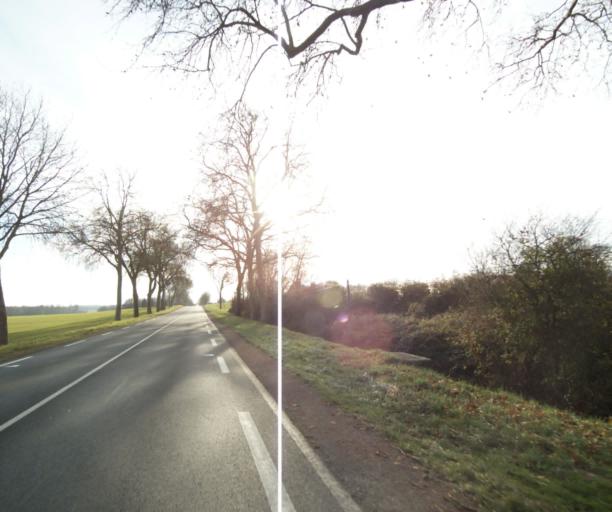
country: FR
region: Poitou-Charentes
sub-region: Departement de la Charente-Maritime
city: Saint-Hilaire-de-Villefranche
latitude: 45.8423
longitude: -0.5346
